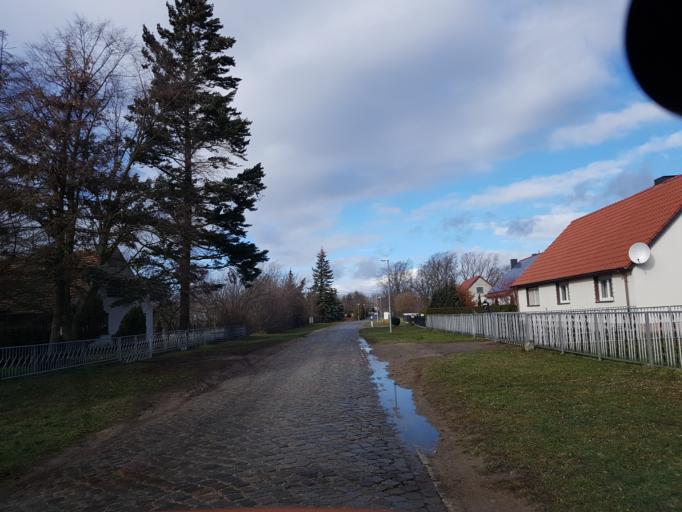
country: DE
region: Brandenburg
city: Muhlberg
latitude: 51.4785
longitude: 13.1974
